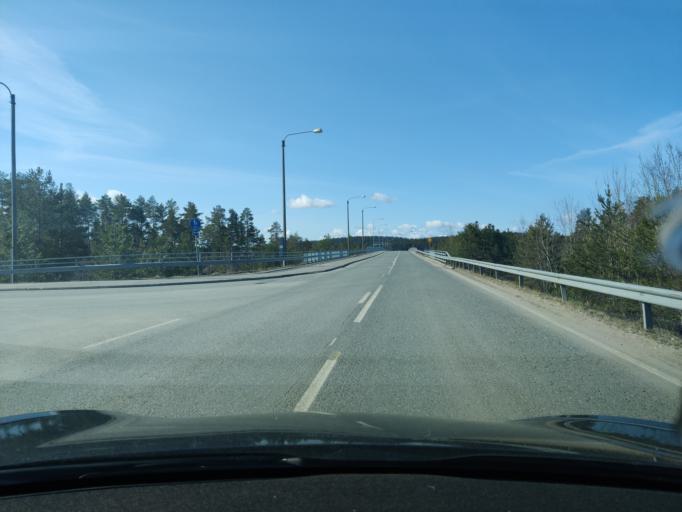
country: FI
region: Northern Savo
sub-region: Kuopio
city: Vehmersalmi
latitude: 62.7711
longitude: 28.0076
